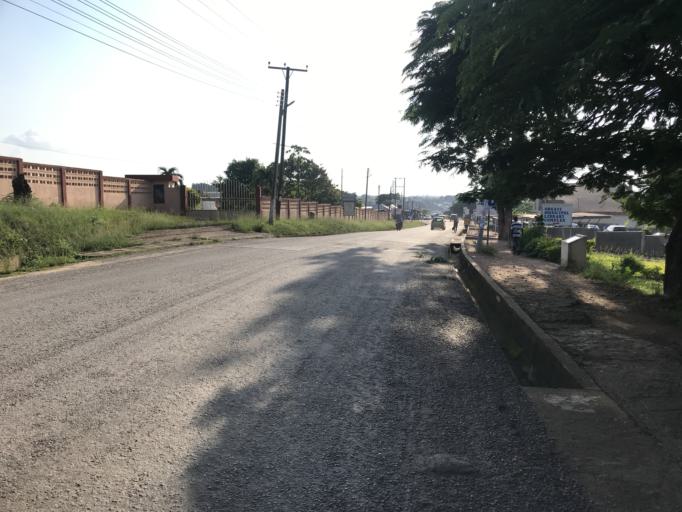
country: GH
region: Ashanti
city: Obuasi
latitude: 6.2037
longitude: -1.6836
